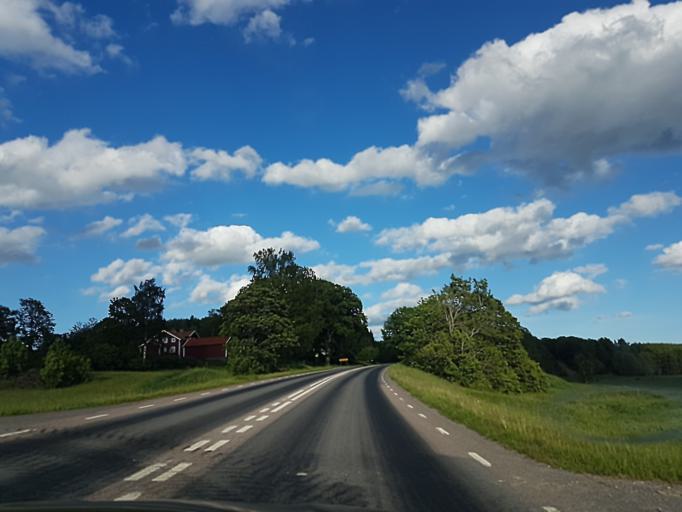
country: SE
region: Soedermanland
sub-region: Nykopings Kommun
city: Stigtomta
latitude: 58.7417
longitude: 16.7840
